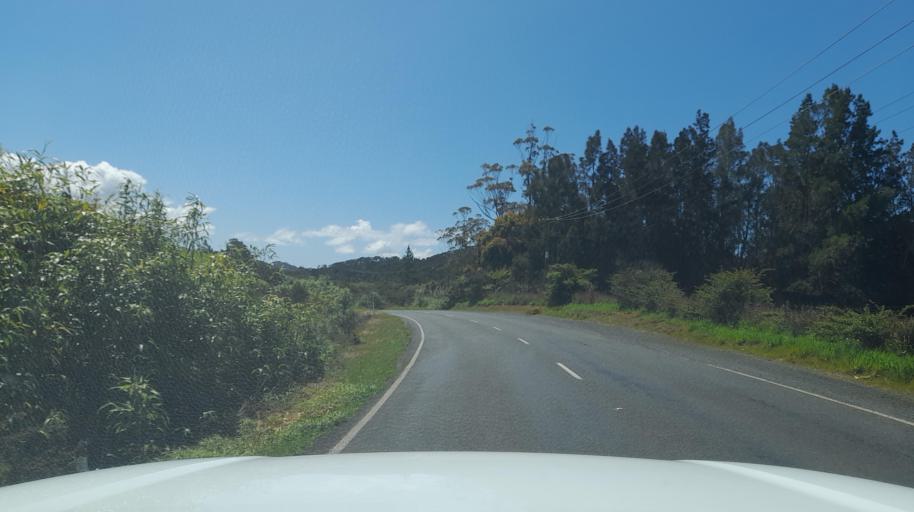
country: NZ
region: Northland
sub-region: Far North District
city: Taipa
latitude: -35.0237
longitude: 173.4756
